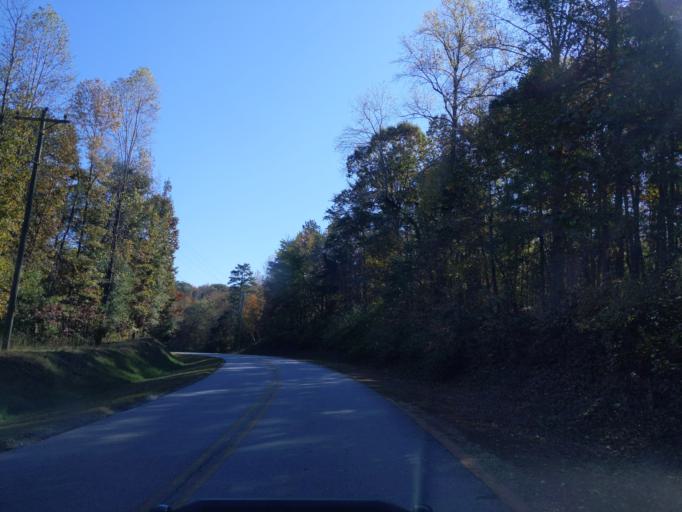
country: US
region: Georgia
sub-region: Franklin County
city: Gumlog
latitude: 34.4948
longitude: -83.0740
